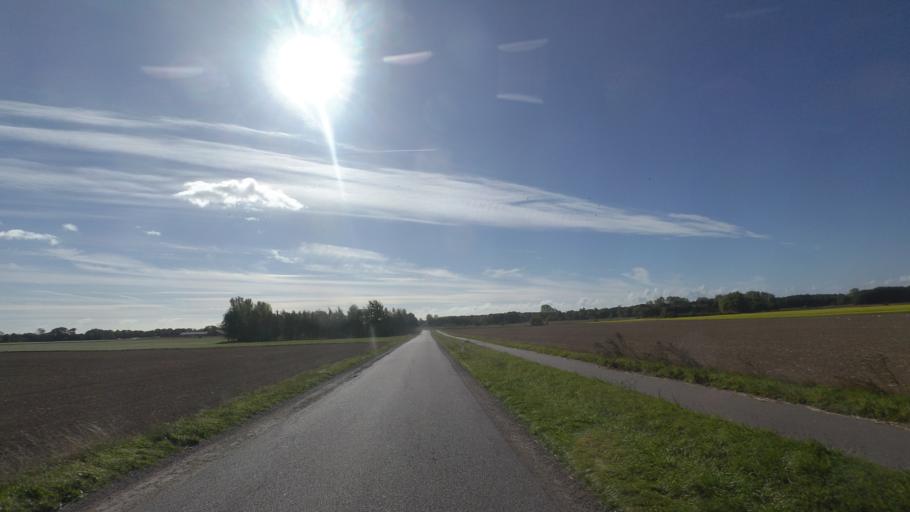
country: DK
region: Capital Region
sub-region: Bornholm Kommune
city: Akirkeby
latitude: 55.0162
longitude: 14.9920
